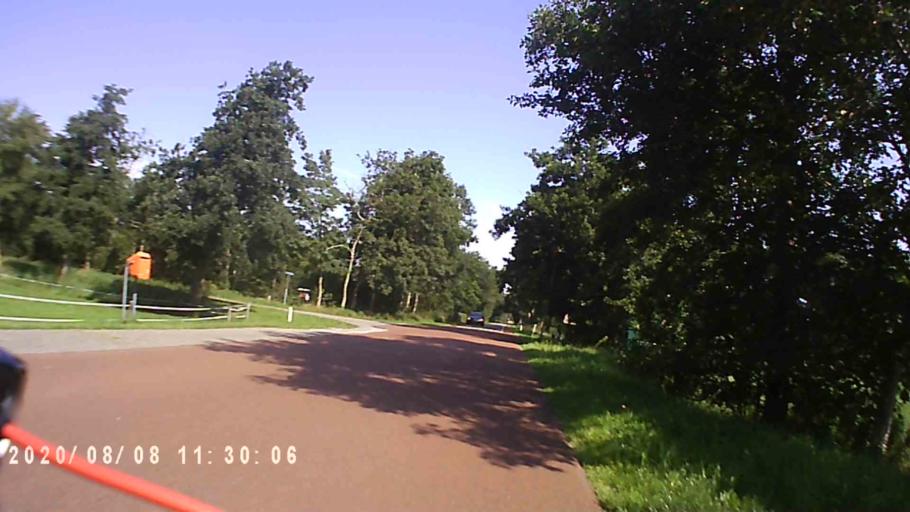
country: NL
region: Groningen
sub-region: Gemeente Leek
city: Leek
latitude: 53.1991
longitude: 6.3870
